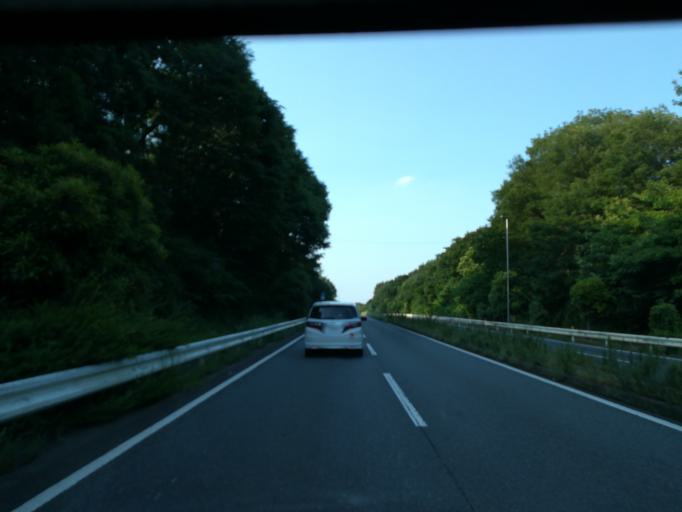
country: JP
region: Saitama
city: Kumagaya
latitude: 36.1061
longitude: 139.3678
